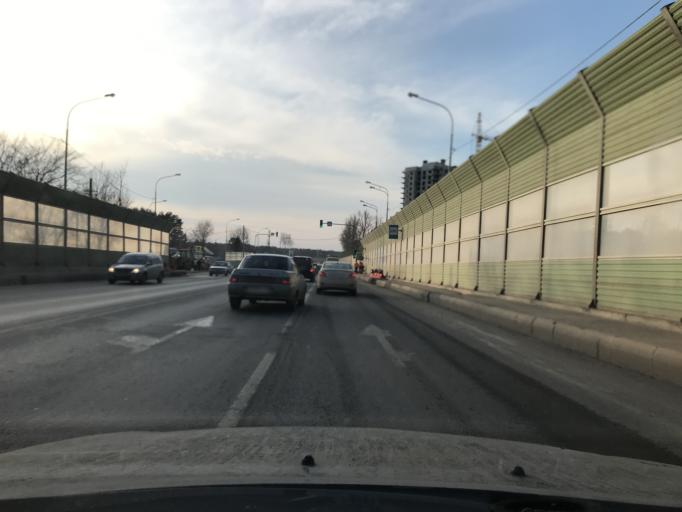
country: RU
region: Kaluga
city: Mstikhino
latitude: 54.5355
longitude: 36.1633
